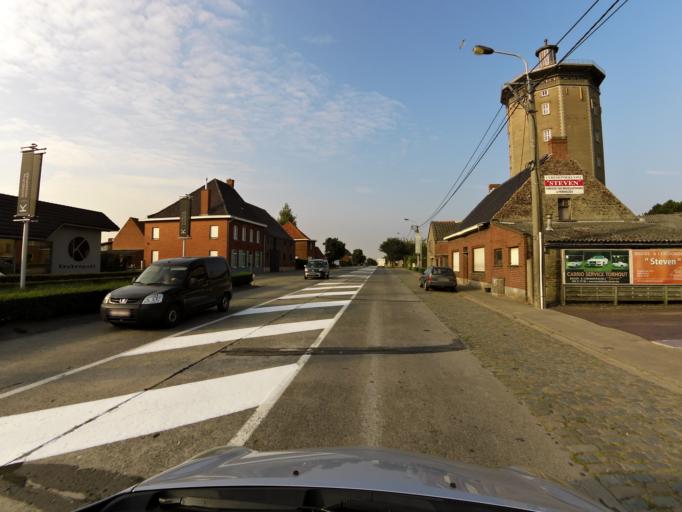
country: BE
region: Flanders
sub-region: Provincie West-Vlaanderen
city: Torhout
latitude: 51.0800
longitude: 3.1141
